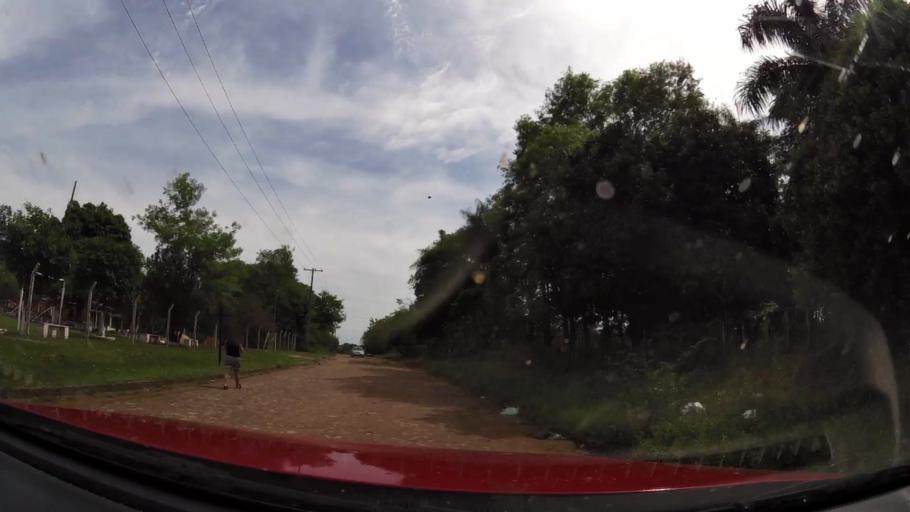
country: PY
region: Central
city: Limpio
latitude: -25.1875
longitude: -57.4737
